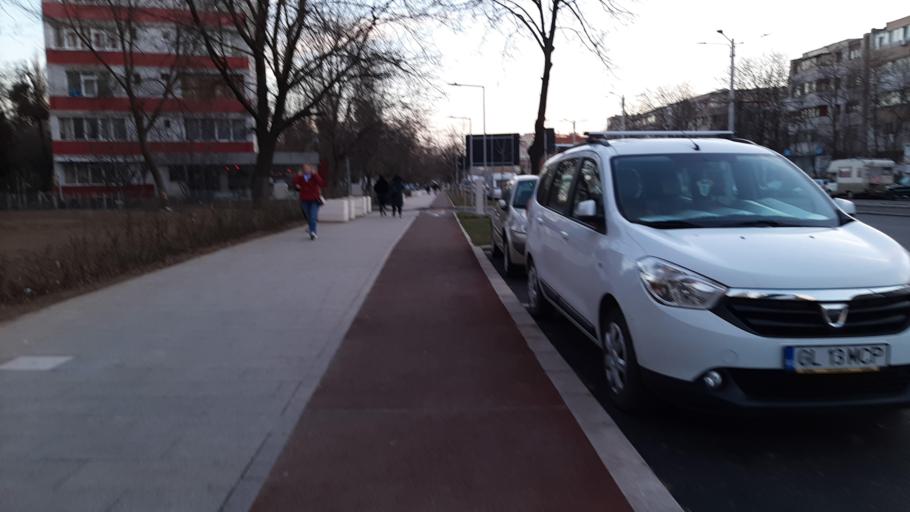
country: RO
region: Galati
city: Galati
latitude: 45.4332
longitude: 28.0256
